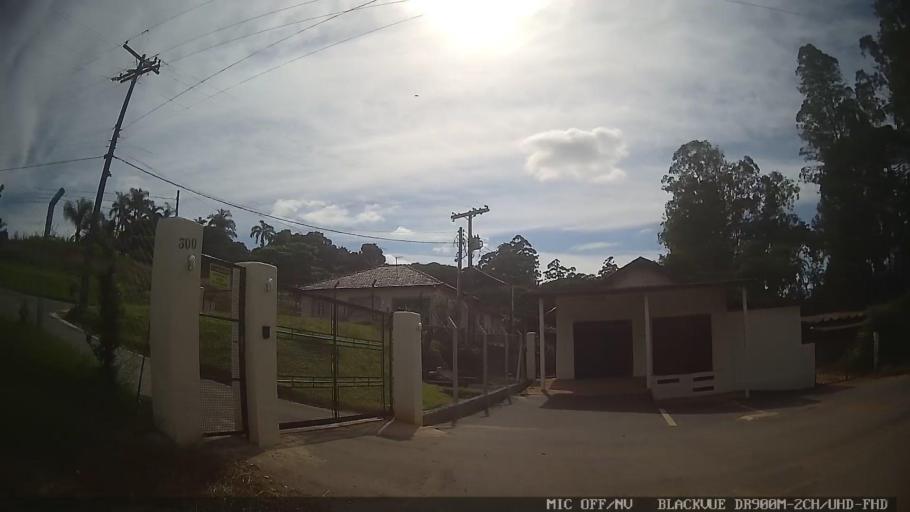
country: BR
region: Sao Paulo
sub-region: Jarinu
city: Jarinu
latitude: -23.0454
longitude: -46.6419
